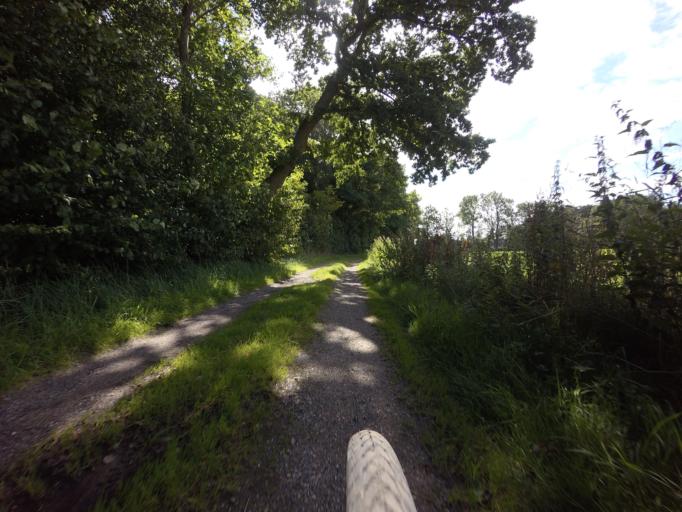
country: DK
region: Central Jutland
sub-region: Norddjurs Kommune
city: Allingabro
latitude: 56.4393
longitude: 10.3488
